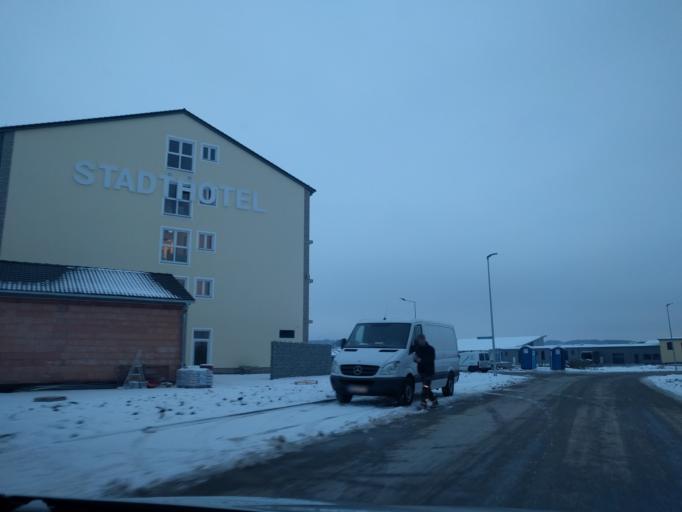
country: DE
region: Bavaria
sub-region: Swabia
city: Donauwoerth
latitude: 48.7070
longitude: 10.7624
